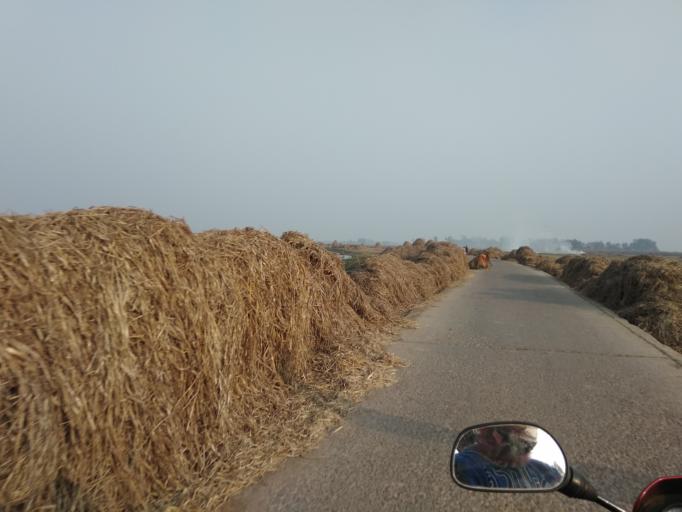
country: BD
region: Rajshahi
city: Ishurdi
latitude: 24.4801
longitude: 89.2378
